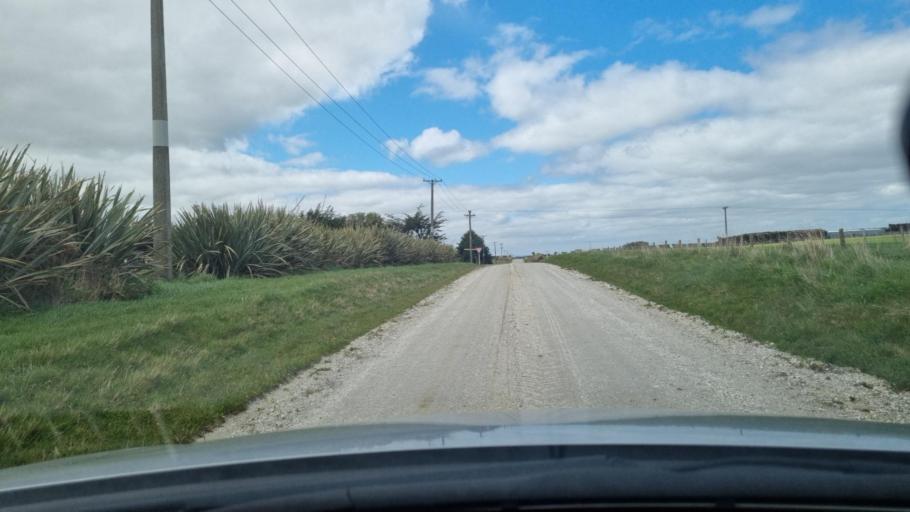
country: NZ
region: Southland
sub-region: Invercargill City
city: Invercargill
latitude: -46.4427
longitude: 168.4571
